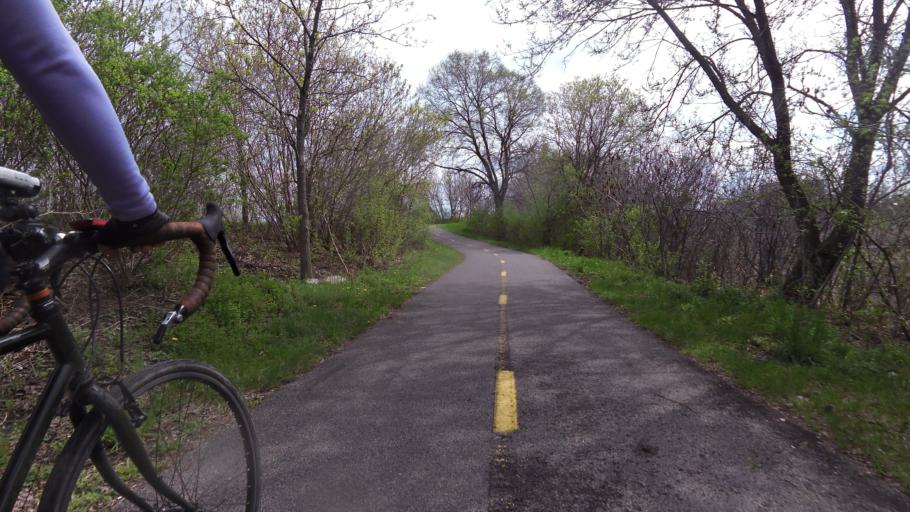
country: CA
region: Ontario
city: Ottawa
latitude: 45.4389
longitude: -75.7248
